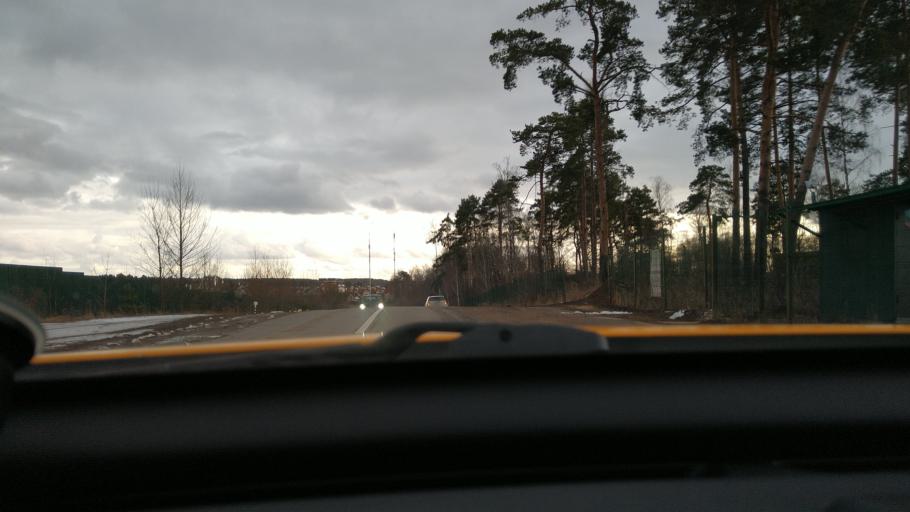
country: RU
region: Moskovskaya
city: Petrovo-Dal'neye
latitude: 55.7558
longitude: 37.2000
